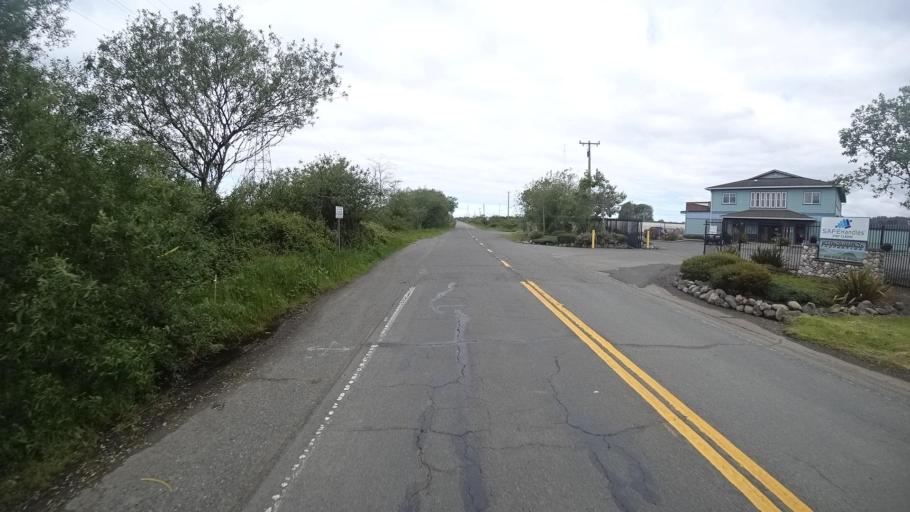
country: US
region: California
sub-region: Humboldt County
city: Arcata
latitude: 40.8519
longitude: -124.0836
